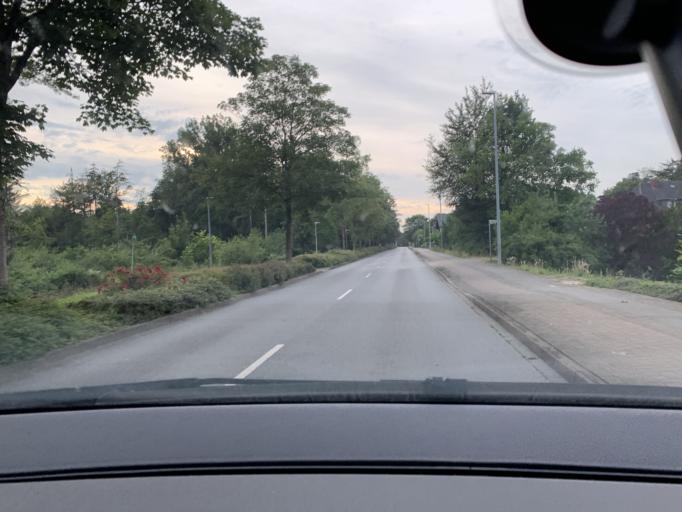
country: DE
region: Schleswig-Holstein
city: Mildstedt
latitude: 54.4737
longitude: 9.0759
